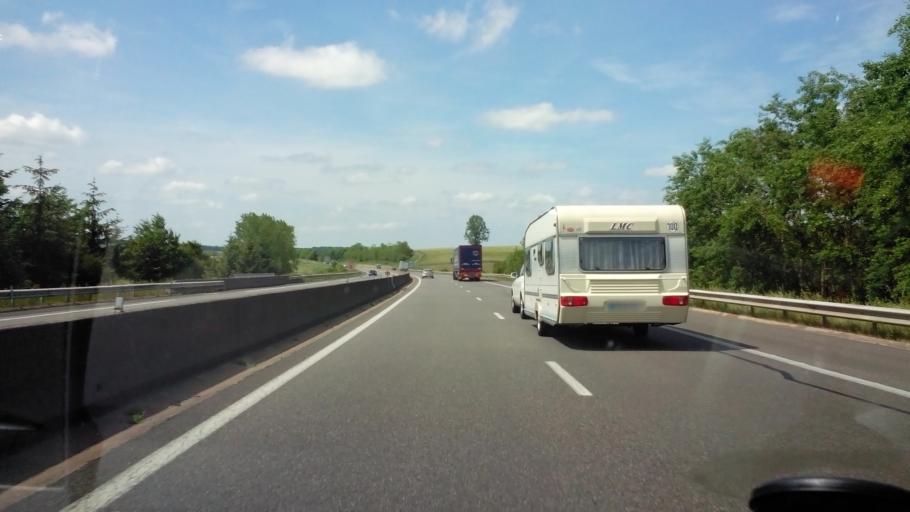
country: FR
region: Lorraine
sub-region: Departement des Vosges
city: Bulgneville
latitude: 48.2169
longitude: 5.8278
